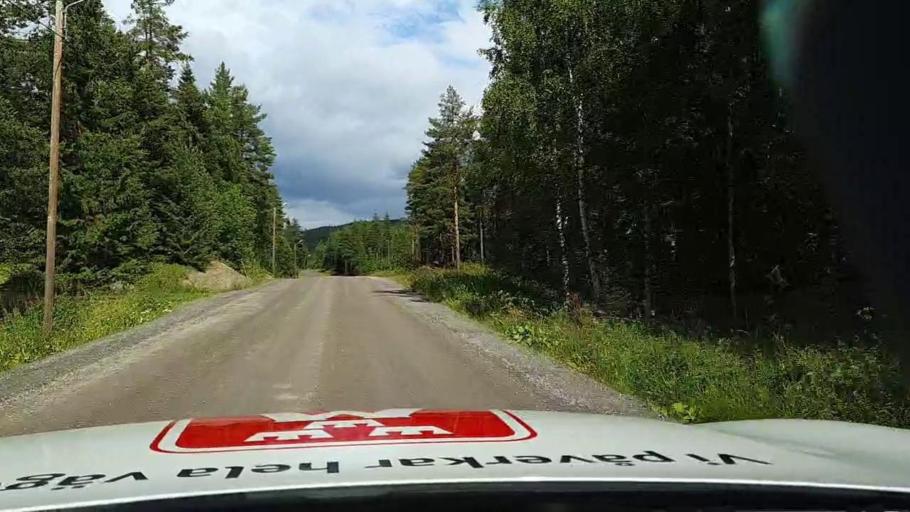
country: SE
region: Vaesternorrland
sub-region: Solleftea Kommun
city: As
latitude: 63.4618
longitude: 16.2699
